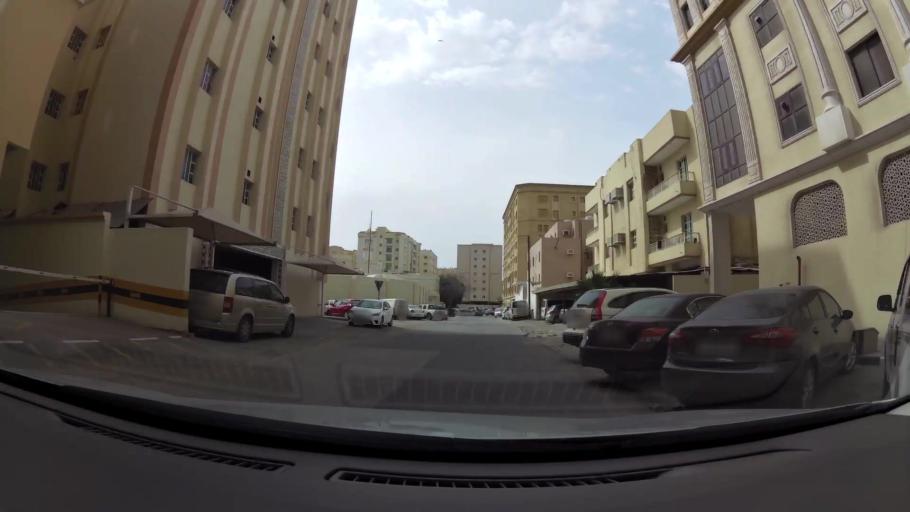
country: QA
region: Baladiyat ad Dawhah
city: Doha
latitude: 25.2894
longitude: 51.4981
